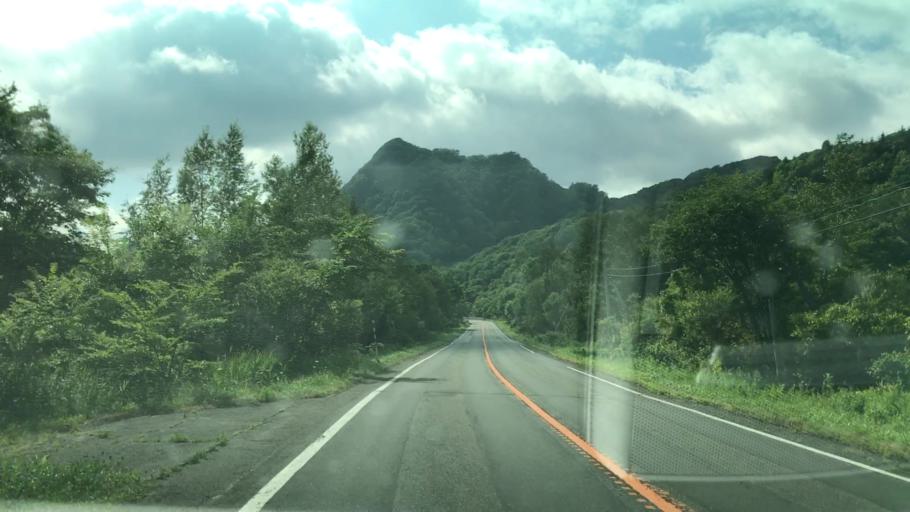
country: JP
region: Hokkaido
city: Shizunai-furukawacho
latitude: 42.8119
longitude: 142.4135
